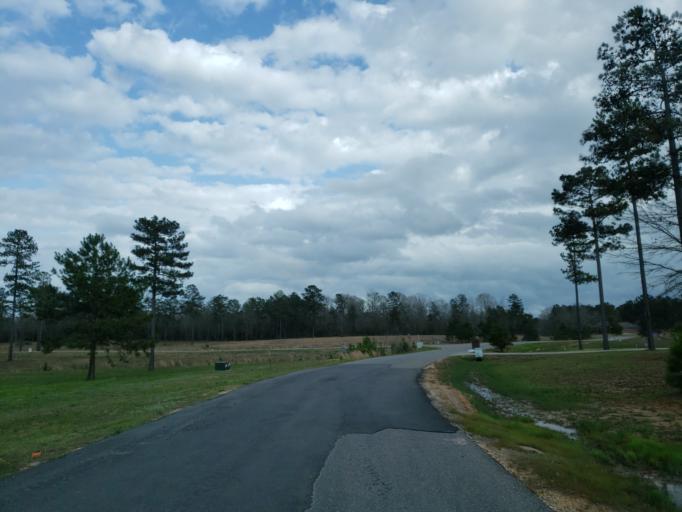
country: US
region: Mississippi
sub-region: Jones County
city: Ellisville
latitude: 31.5640
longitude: -89.2500
